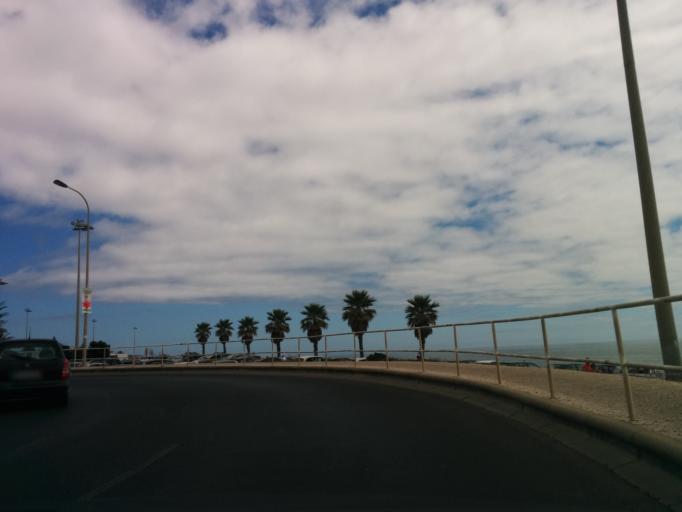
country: PT
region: Lisbon
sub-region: Cascais
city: Parede
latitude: 38.6931
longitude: -9.3674
